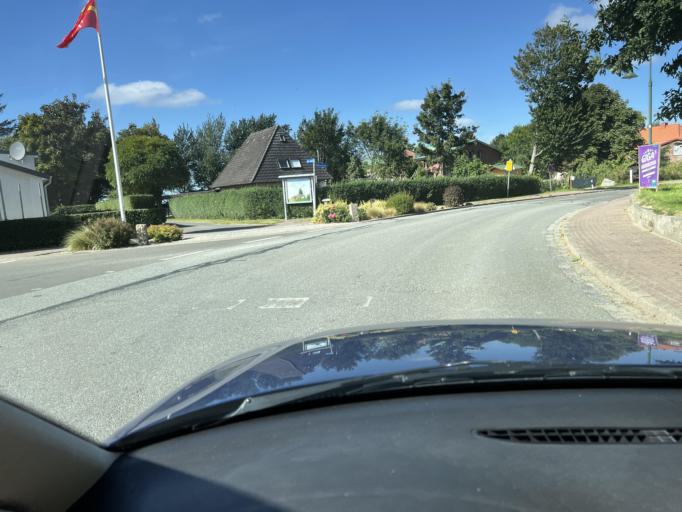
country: DE
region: Schleswig-Holstein
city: Norddeich
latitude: 54.2181
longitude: 8.9004
